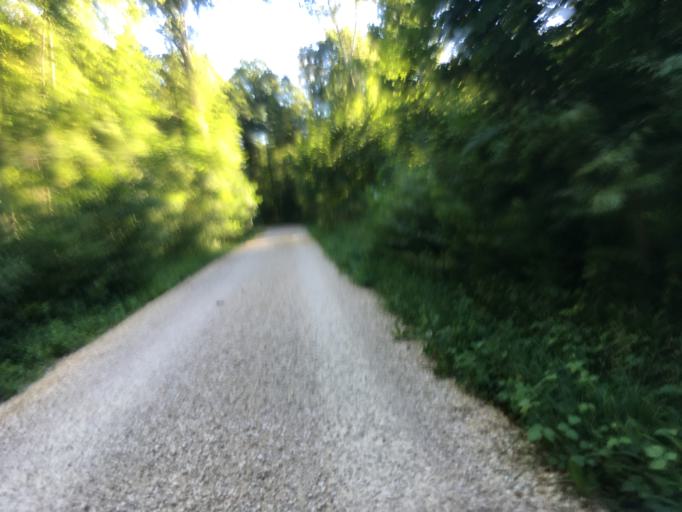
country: CH
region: Fribourg
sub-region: See District
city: Murten
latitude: 46.9432
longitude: 7.1373
